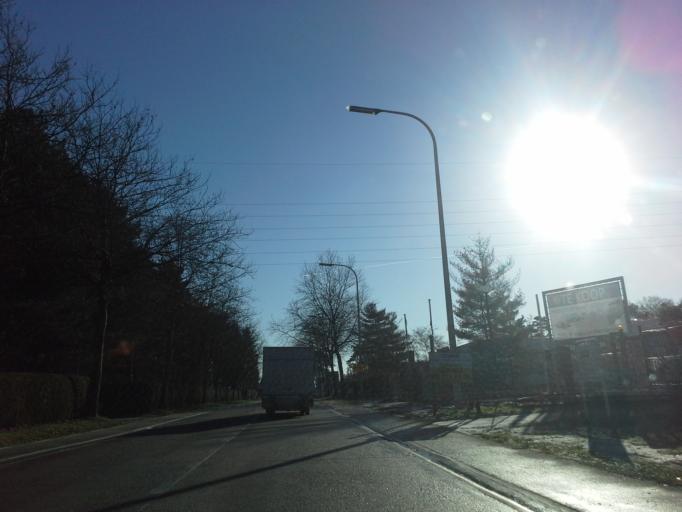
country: BE
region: Flanders
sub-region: Provincie Antwerpen
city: Herentals
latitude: 51.1557
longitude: 4.8034
